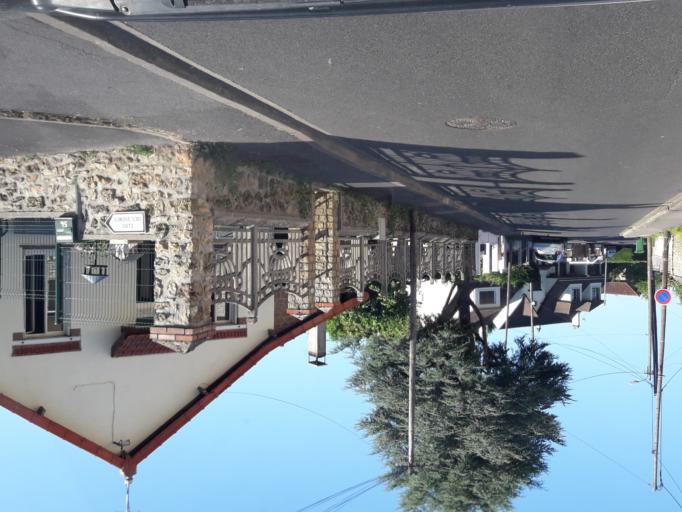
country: FR
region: Ile-de-France
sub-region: Departement de l'Essonne
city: Saint-Vrain
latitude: 48.5420
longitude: 2.3276
